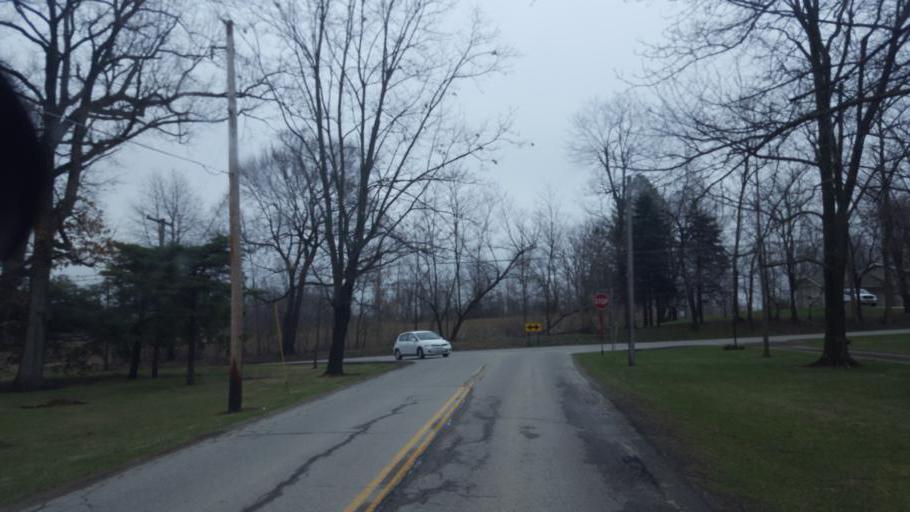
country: US
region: Ohio
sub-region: Richland County
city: Lexington
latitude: 40.6849
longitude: -82.5215
